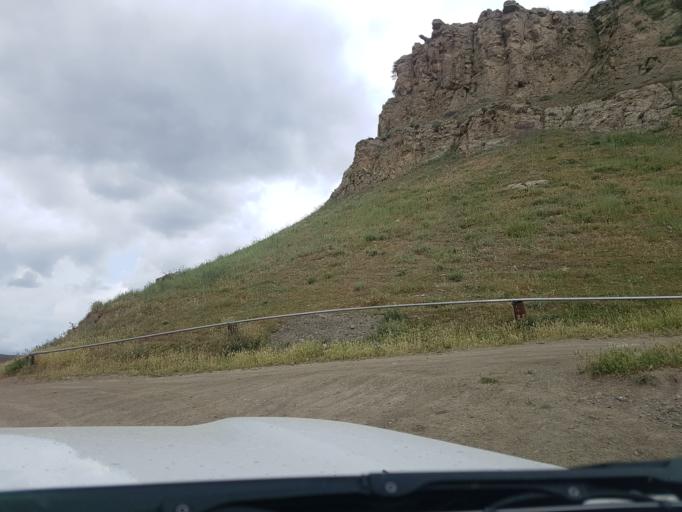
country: TM
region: Ahal
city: Baharly
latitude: 38.2019
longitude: 57.0042
